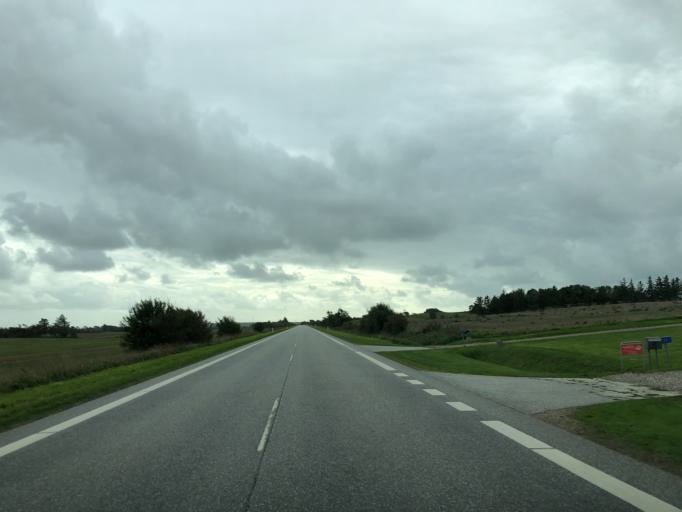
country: DK
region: North Denmark
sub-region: Thisted Kommune
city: Hurup
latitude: 56.8086
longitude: 8.4812
